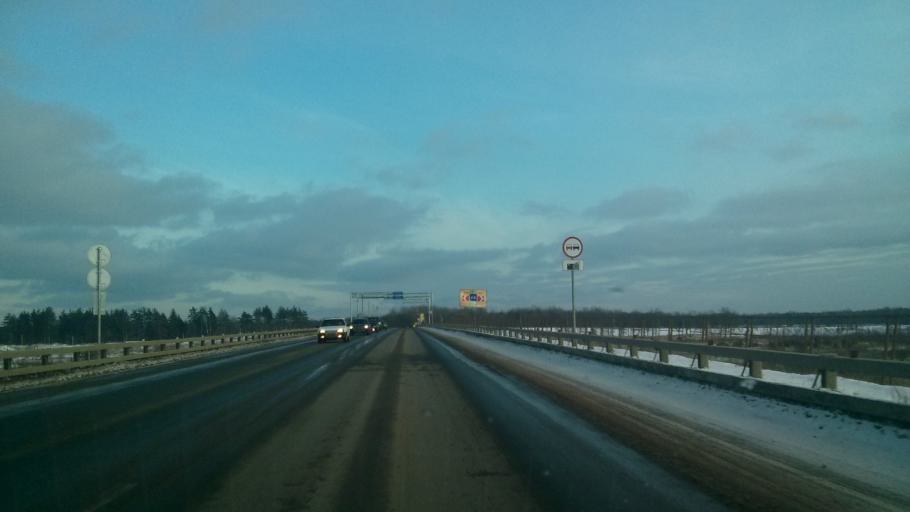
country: RU
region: Nizjnij Novgorod
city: Navashino
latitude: 55.5867
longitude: 42.1413
